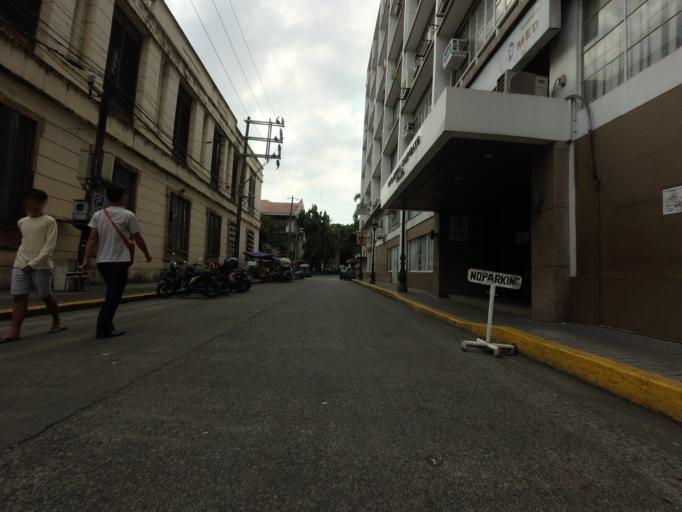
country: PH
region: Metro Manila
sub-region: City of Manila
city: Port Area
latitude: 14.5880
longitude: 120.9780
